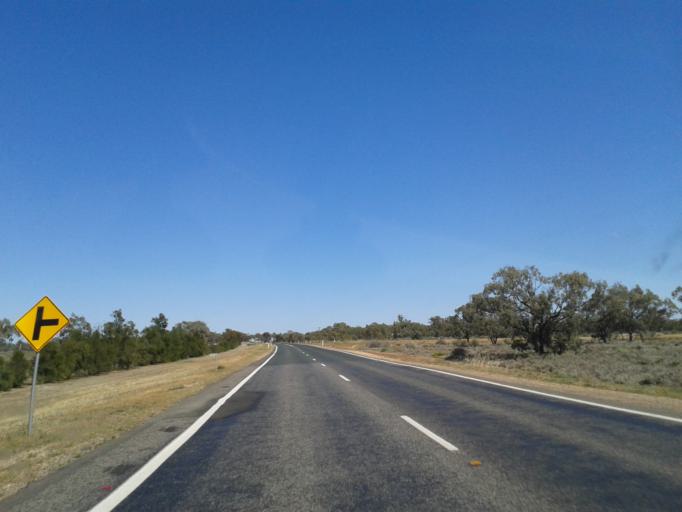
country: AU
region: New South Wales
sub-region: Wentworth
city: Dareton
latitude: -34.1092
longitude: 141.9360
